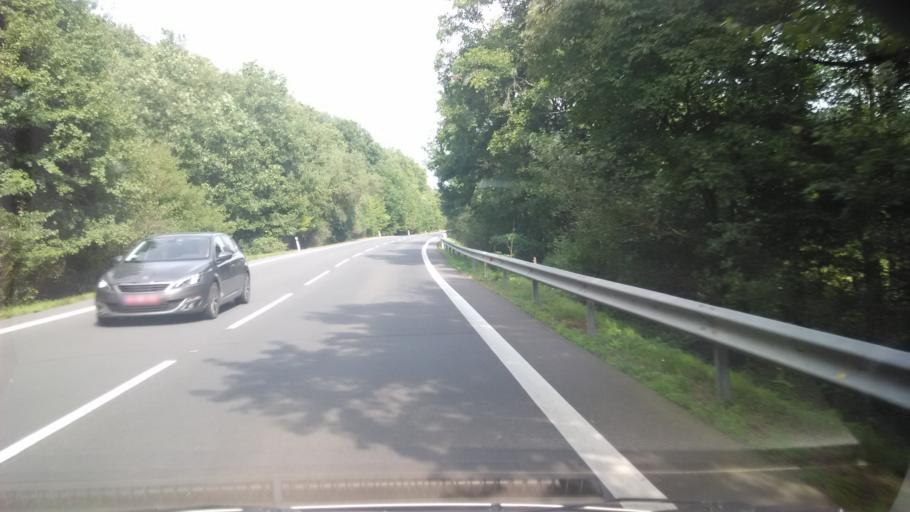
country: SK
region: Banskobystricky
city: Dudince
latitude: 48.2500
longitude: 18.9702
